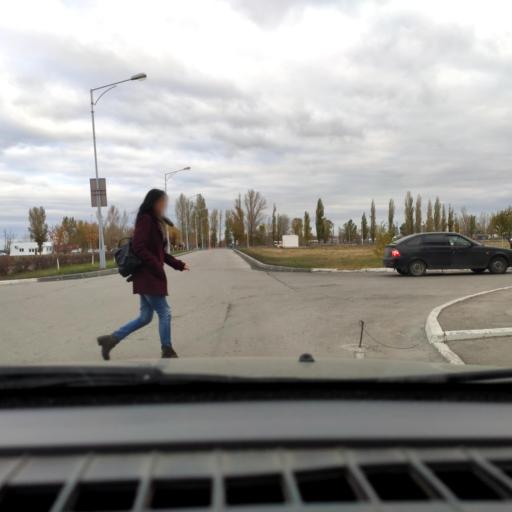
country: RU
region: Samara
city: Podstepki
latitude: 53.5570
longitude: 49.2157
